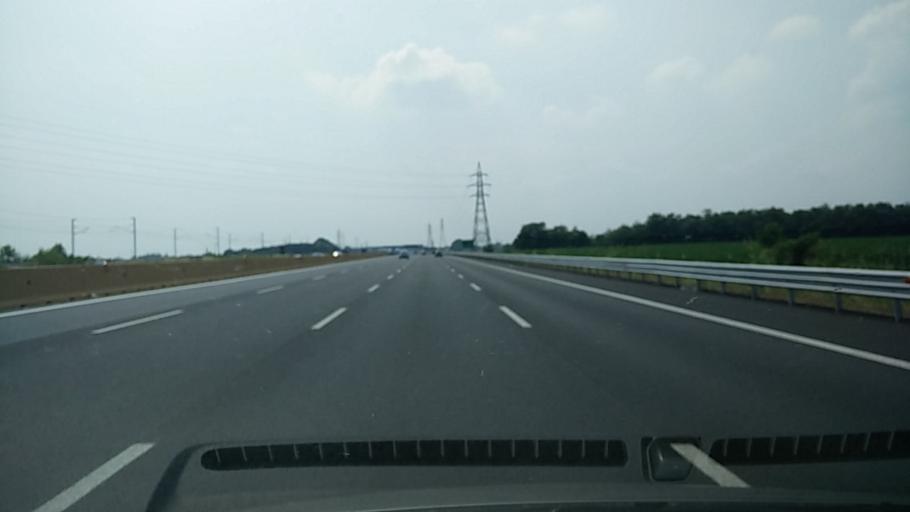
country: IT
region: Lombardy
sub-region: Citta metropolitana di Milano
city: Ossona
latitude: 45.4959
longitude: 8.8965
